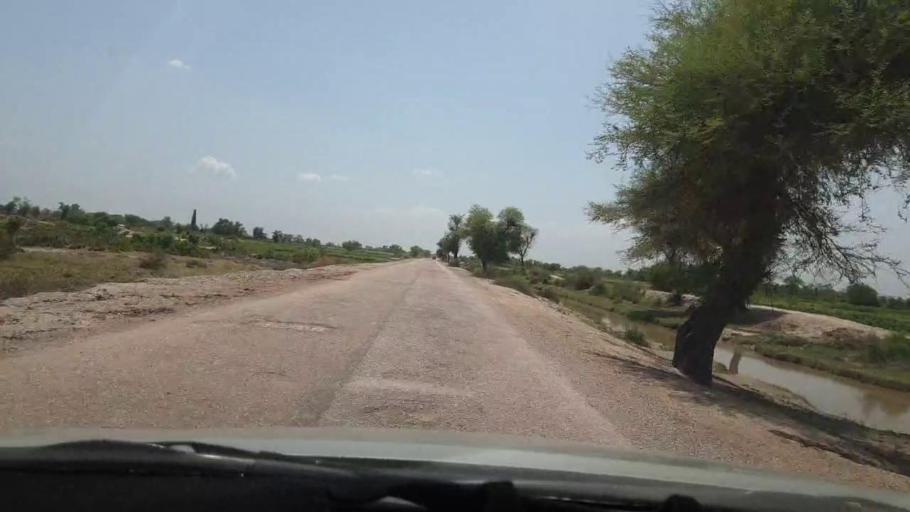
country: PK
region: Sindh
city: Pano Aqil
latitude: 27.7241
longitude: 69.1779
